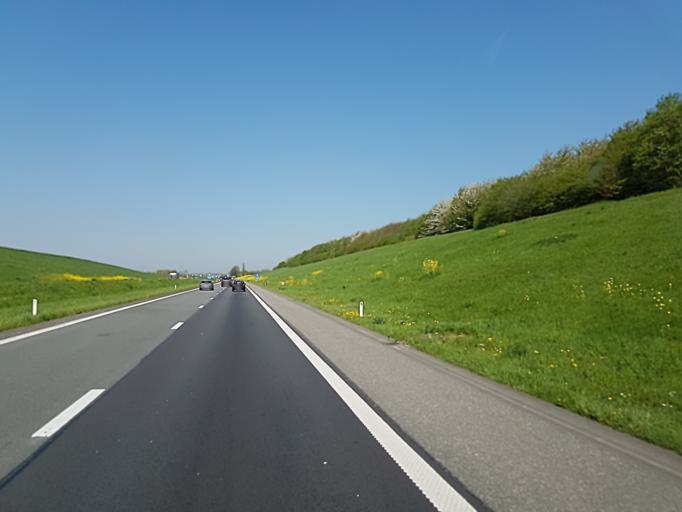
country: BE
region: Flanders
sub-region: Provincie West-Vlaanderen
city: Zonnebeke
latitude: 50.8507
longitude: 2.9784
